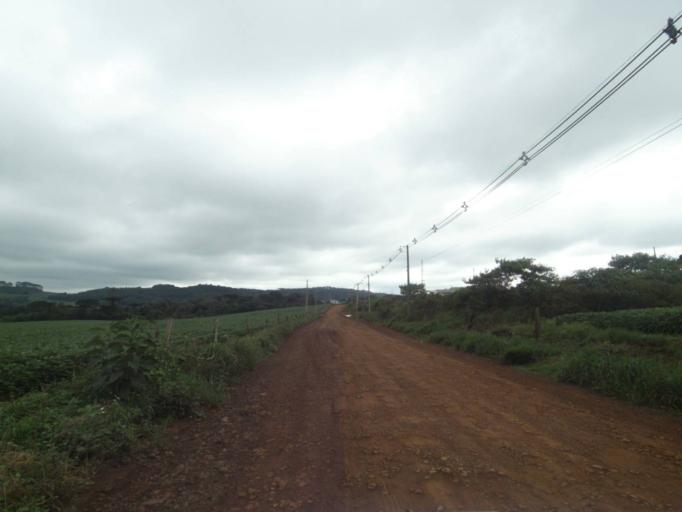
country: BR
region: Parana
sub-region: Pitanga
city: Pitanga
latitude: -24.9409
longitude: -51.8788
